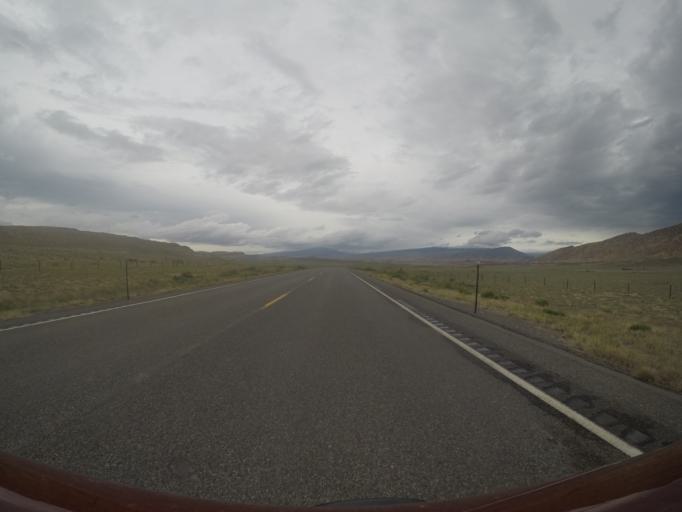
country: US
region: Wyoming
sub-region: Big Horn County
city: Lovell
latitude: 44.9227
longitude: -108.2977
